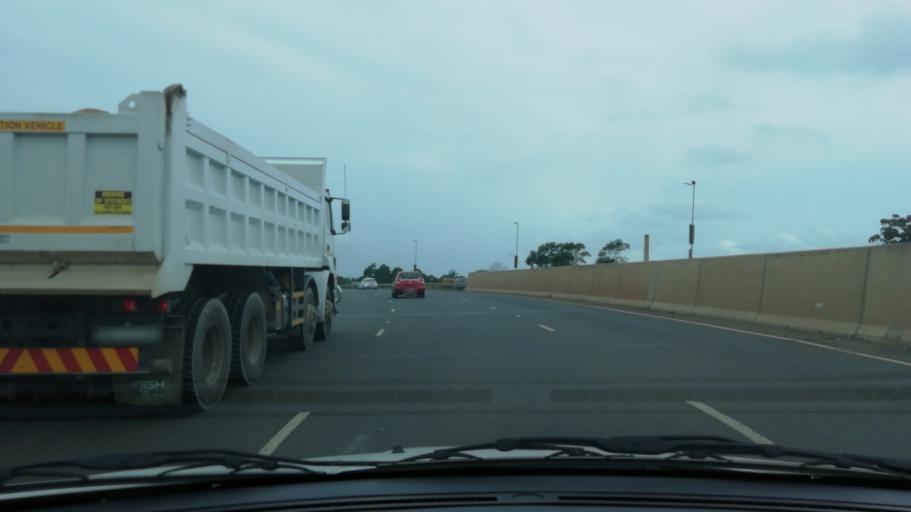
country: ZA
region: KwaZulu-Natal
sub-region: uThungulu District Municipality
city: Empangeni
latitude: -28.7666
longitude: 31.9106
